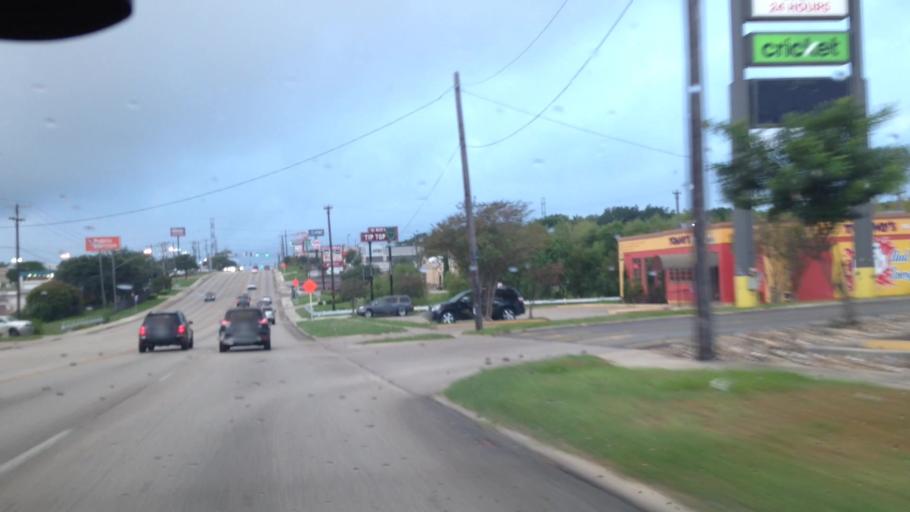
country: US
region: Texas
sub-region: Bexar County
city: Live Oak
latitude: 29.5674
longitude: -98.3861
